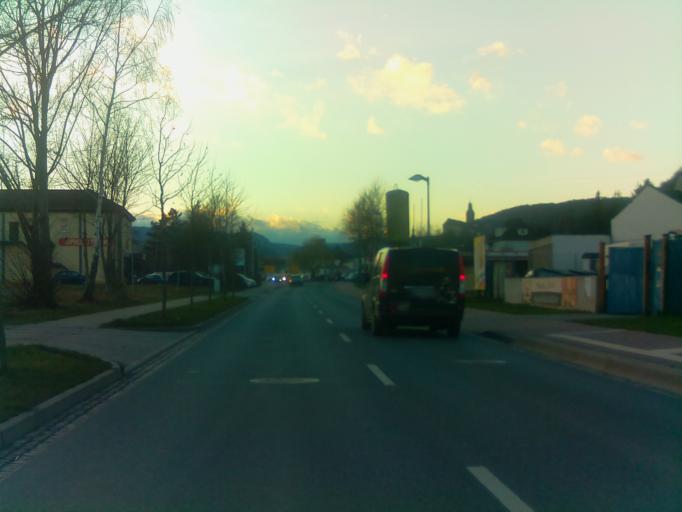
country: DE
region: Thuringia
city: Rudolstadt
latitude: 50.7225
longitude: 11.3585
